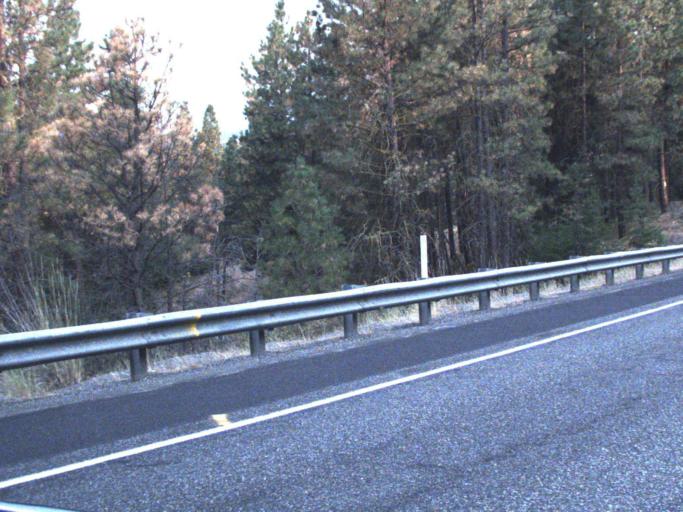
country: US
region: Washington
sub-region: Kittitas County
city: Cle Elum
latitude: 47.1911
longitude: -120.7063
